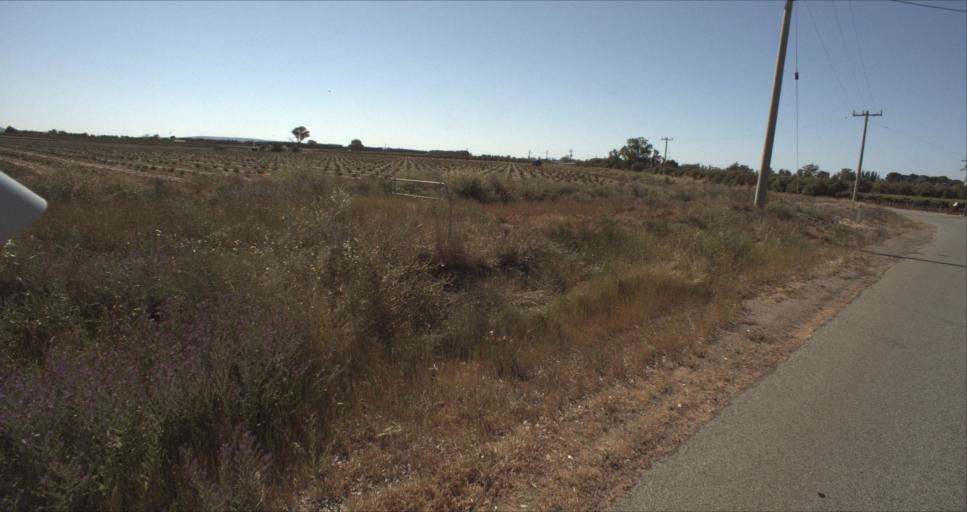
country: AU
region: New South Wales
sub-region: Leeton
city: Leeton
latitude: -34.5386
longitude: 146.3352
